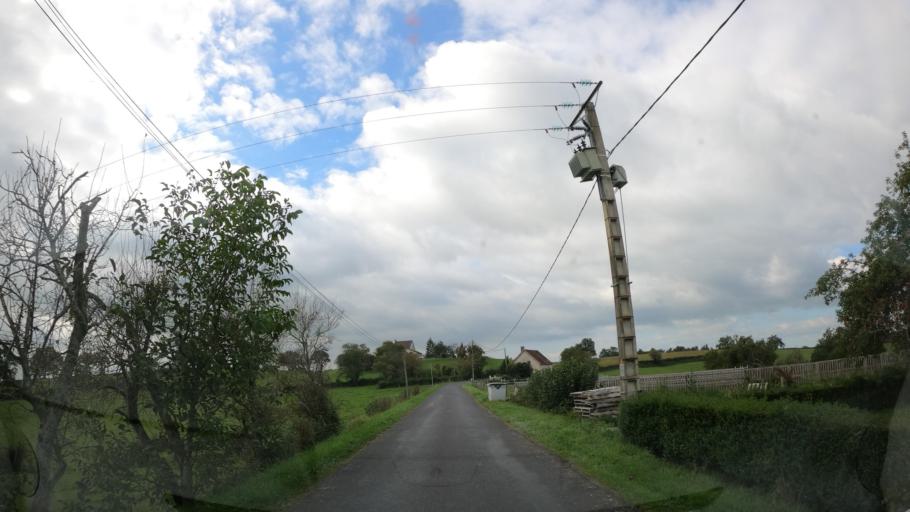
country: FR
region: Auvergne
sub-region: Departement de l'Allier
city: Lapalisse
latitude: 46.3443
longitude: 3.6350
